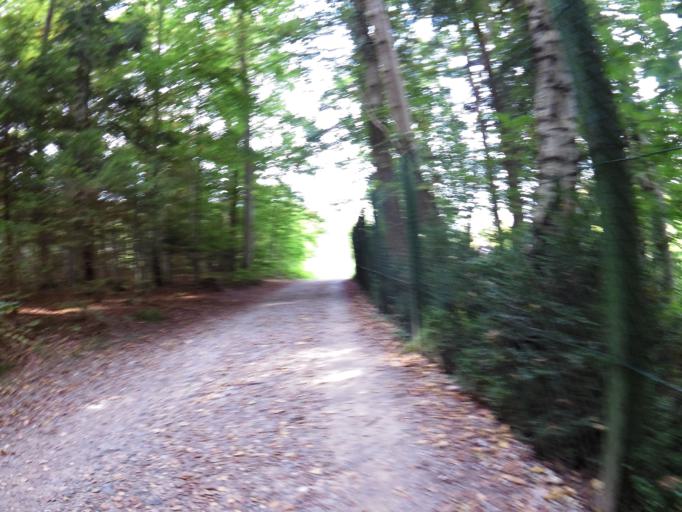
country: DE
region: Bavaria
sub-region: Upper Bavaria
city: Pocking
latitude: 47.9542
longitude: 11.3101
